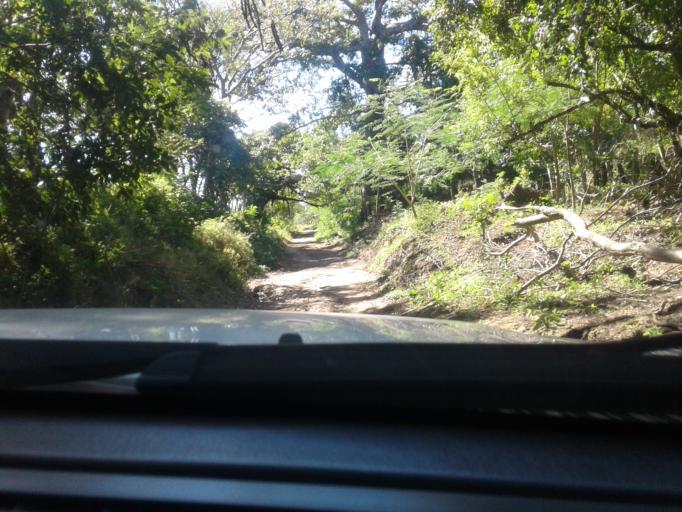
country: NI
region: Carazo
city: Santa Teresa
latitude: 11.7857
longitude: -86.1860
